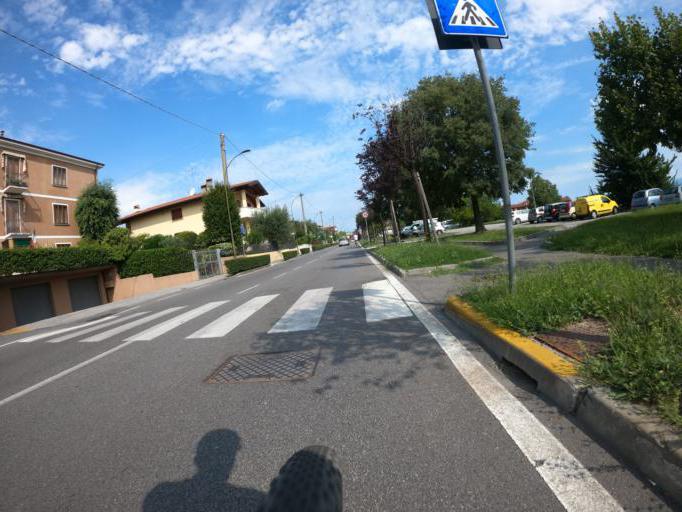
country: IT
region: Lombardy
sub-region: Provincia di Brescia
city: Desenzano del Garda
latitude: 45.4521
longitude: 10.5661
